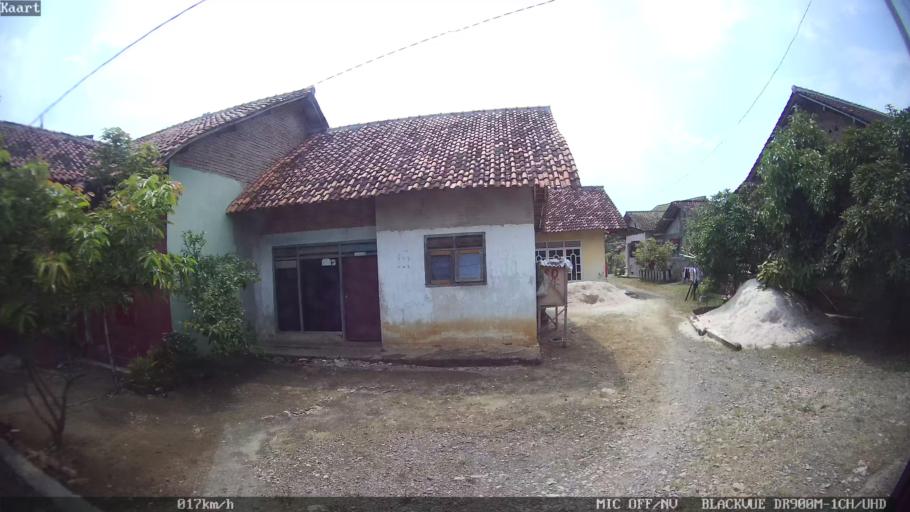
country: ID
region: Lampung
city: Gadingrejo
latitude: -5.3659
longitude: 105.0590
